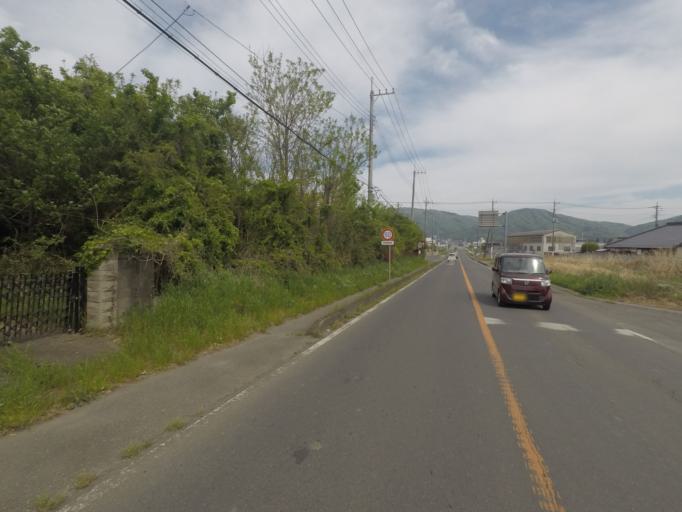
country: JP
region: Ibaraki
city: Makabe
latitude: 36.2803
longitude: 140.0837
